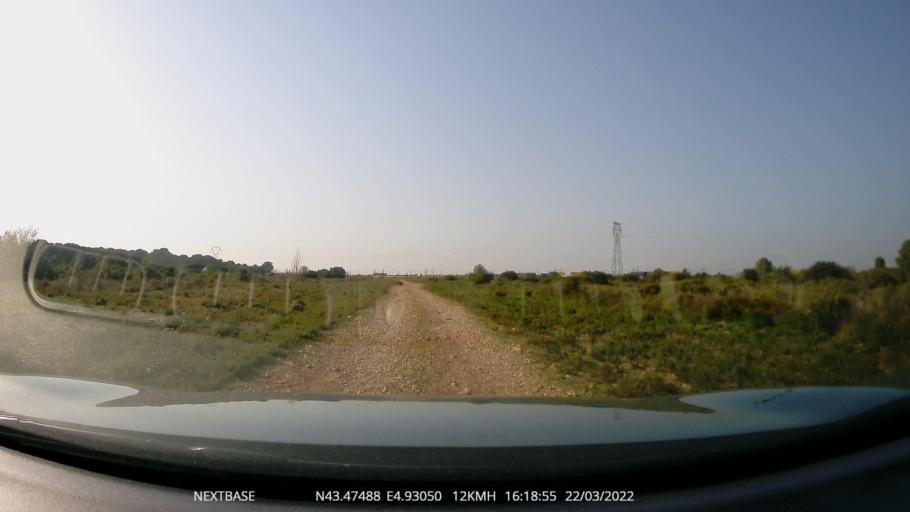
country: FR
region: Provence-Alpes-Cote d'Azur
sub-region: Departement des Bouches-du-Rhone
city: Fos-sur-Mer
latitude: 43.4749
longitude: 4.9305
